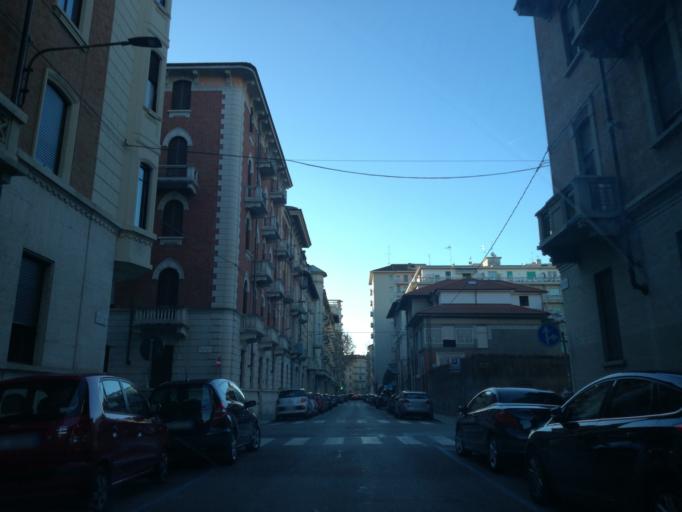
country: IT
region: Piedmont
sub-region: Provincia di Torino
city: Turin
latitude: 45.0780
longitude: 7.6583
